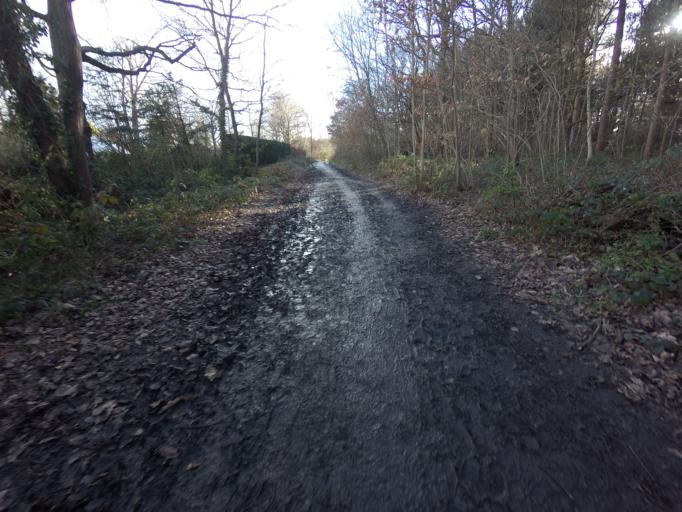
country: GB
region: England
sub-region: Greater London
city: Bexley
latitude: 51.4248
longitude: 0.1617
